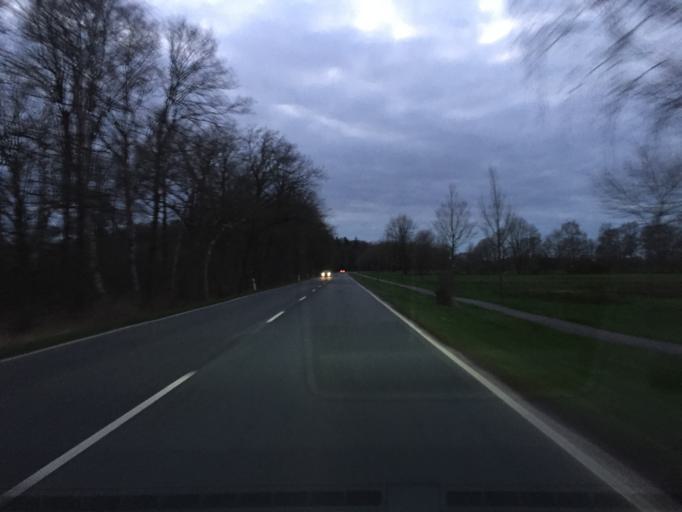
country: DE
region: Lower Saxony
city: Heemsen
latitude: 52.6617
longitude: 9.2657
